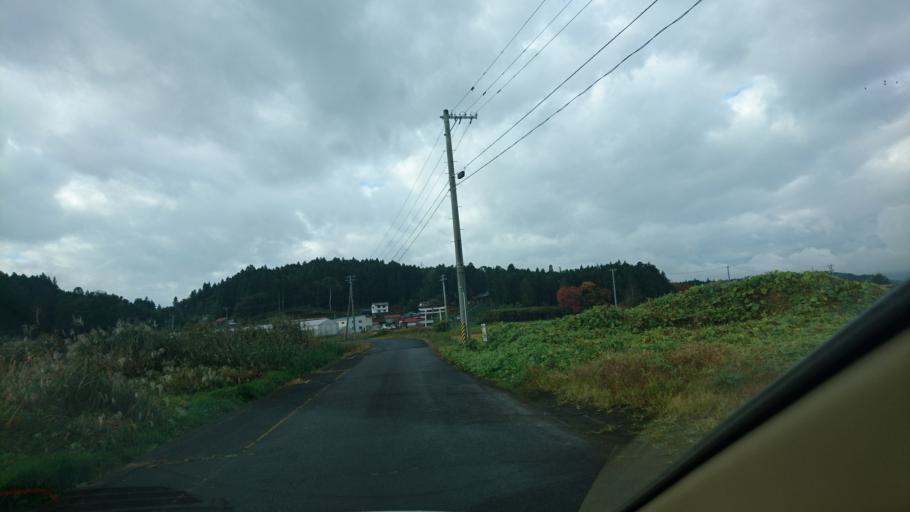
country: JP
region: Iwate
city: Ichinoseki
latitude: 38.7972
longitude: 140.9888
